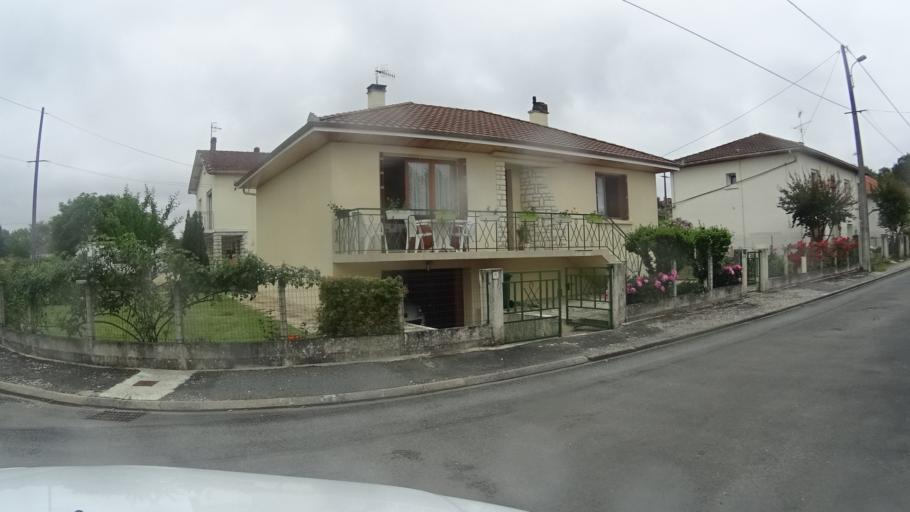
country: FR
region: Aquitaine
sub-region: Departement de la Dordogne
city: Mussidan
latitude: 45.0317
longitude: 0.3656
